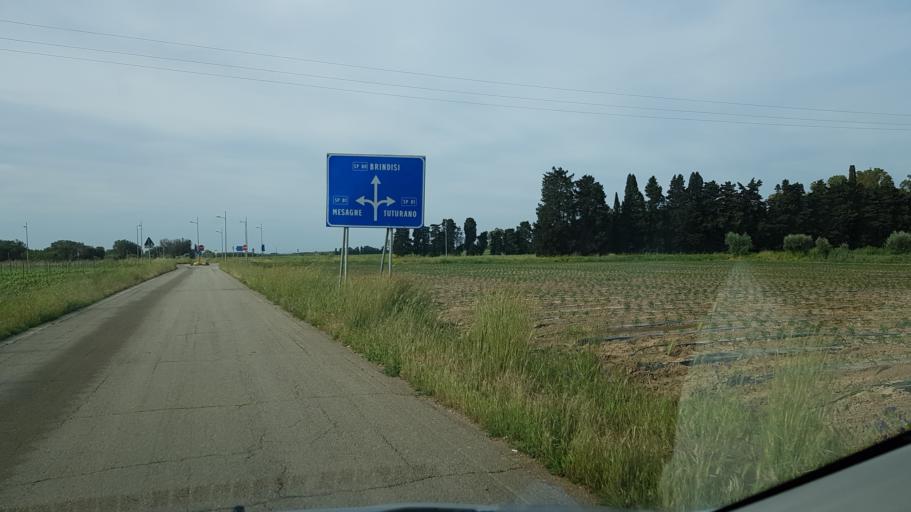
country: IT
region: Apulia
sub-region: Provincia di Brindisi
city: Tuturano
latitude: 40.5490
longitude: 17.8900
